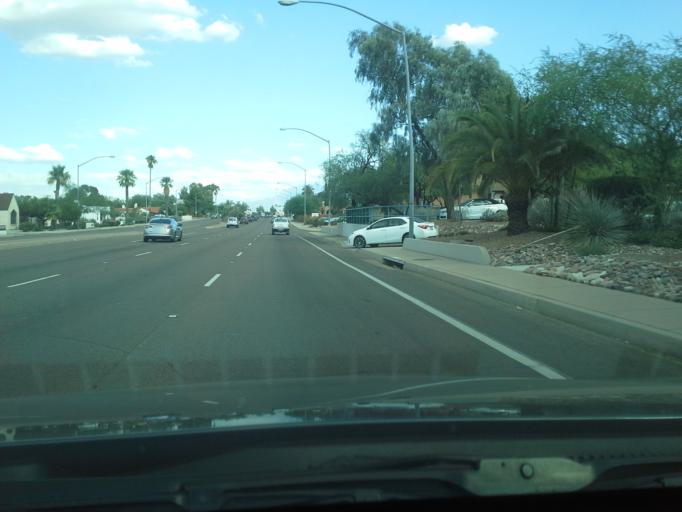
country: US
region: Arizona
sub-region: Pima County
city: Tucson
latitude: 32.2360
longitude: -110.9391
